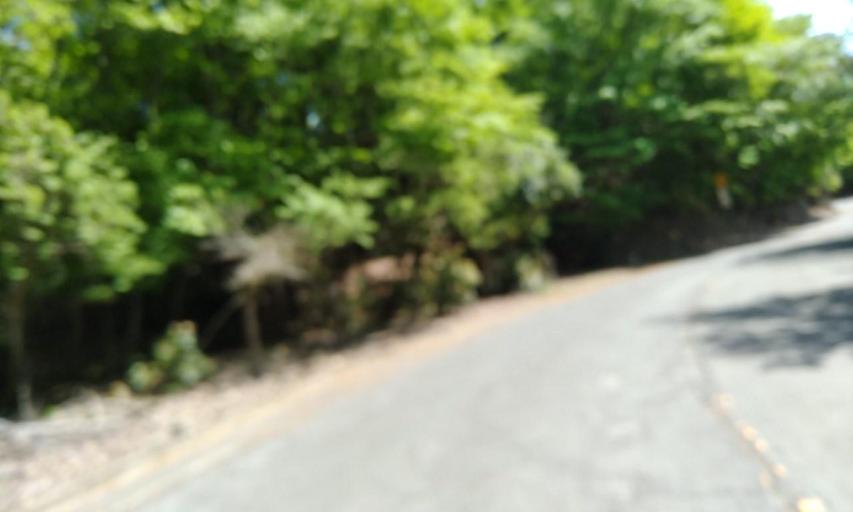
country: JP
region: Fukui
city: Obama
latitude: 35.5590
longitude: 135.7283
